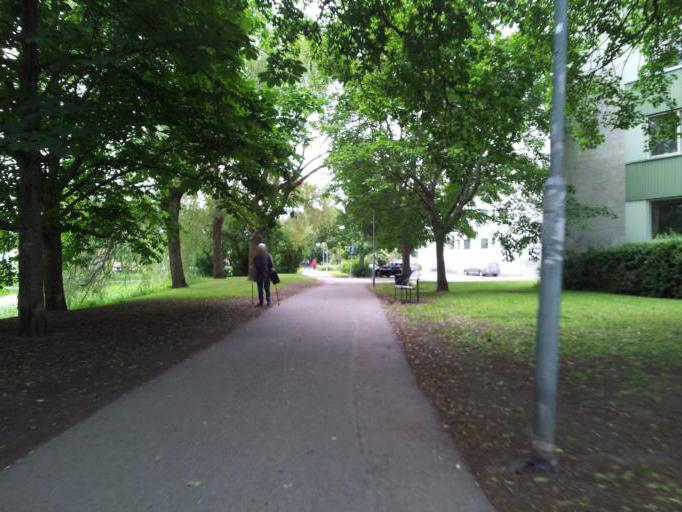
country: SE
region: Uppsala
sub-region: Uppsala Kommun
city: Uppsala
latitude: 59.8632
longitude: 17.6304
